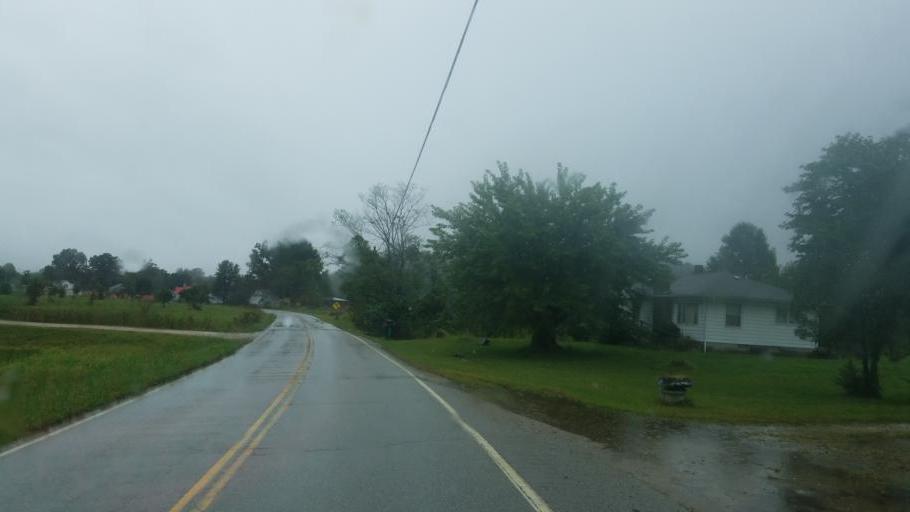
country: US
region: Kentucky
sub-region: Greenup County
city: South Shore
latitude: 38.6845
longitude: -82.9183
